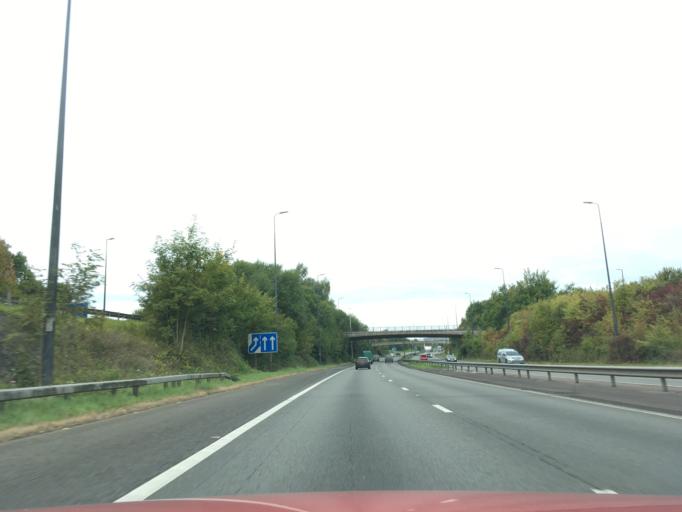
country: GB
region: Wales
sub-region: Monmouthshire
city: Magor
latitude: 51.5863
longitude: -2.8360
